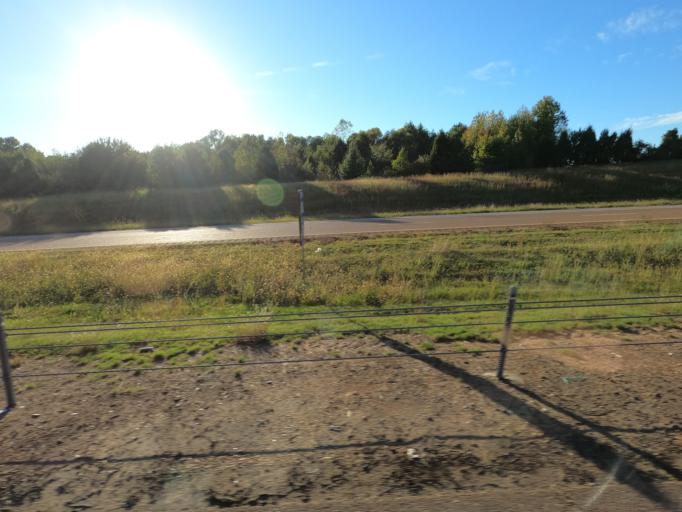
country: US
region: Tennessee
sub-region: Shelby County
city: Arlington
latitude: 35.2694
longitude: -89.6787
